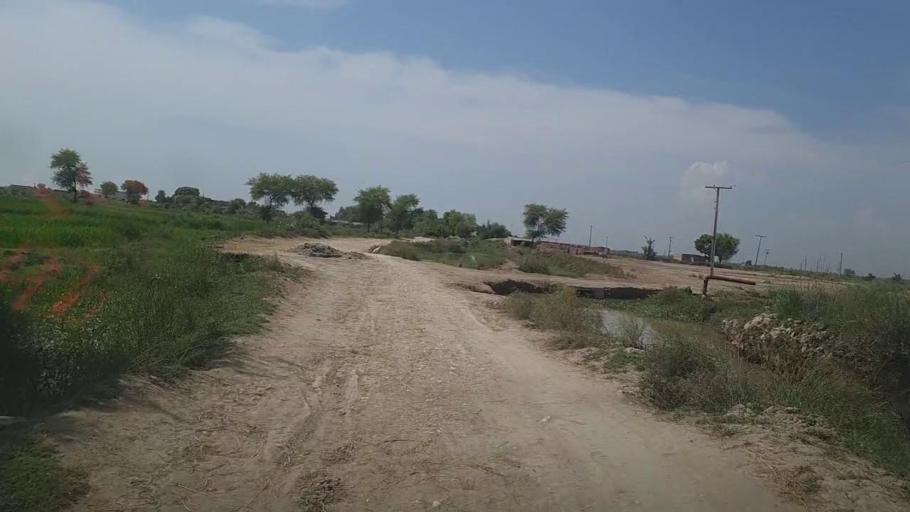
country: PK
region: Sindh
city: Kandhkot
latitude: 28.3109
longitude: 69.2305
